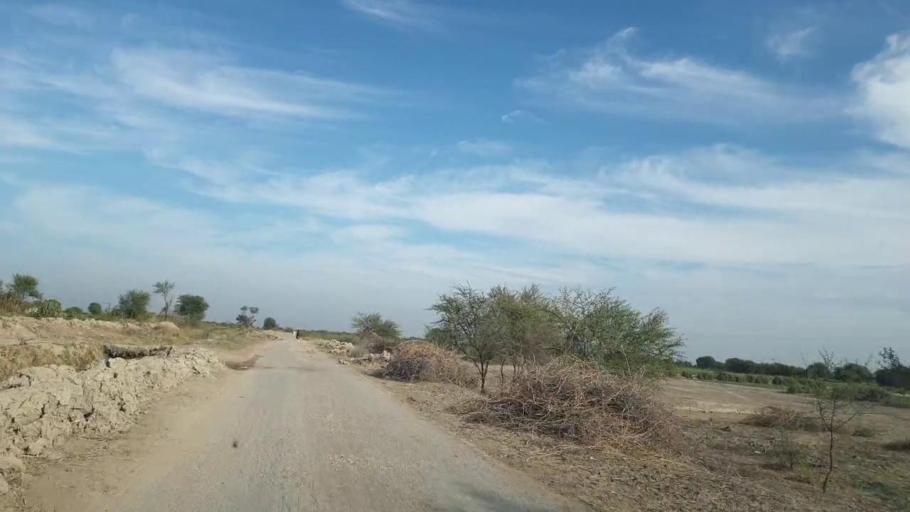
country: PK
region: Sindh
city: Pithoro
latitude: 25.6455
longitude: 69.3583
